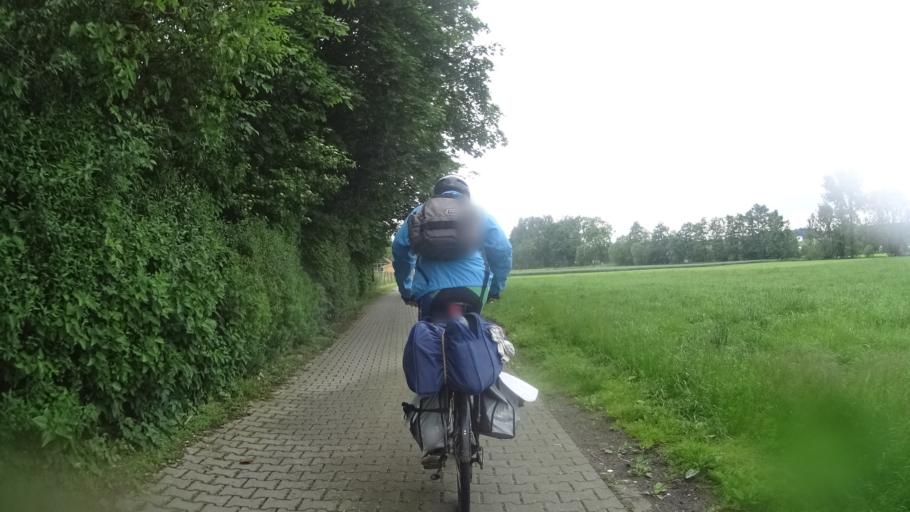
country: DE
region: Bavaria
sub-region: Lower Bavaria
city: Hebertsfelden
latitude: 48.4101
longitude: 12.8044
